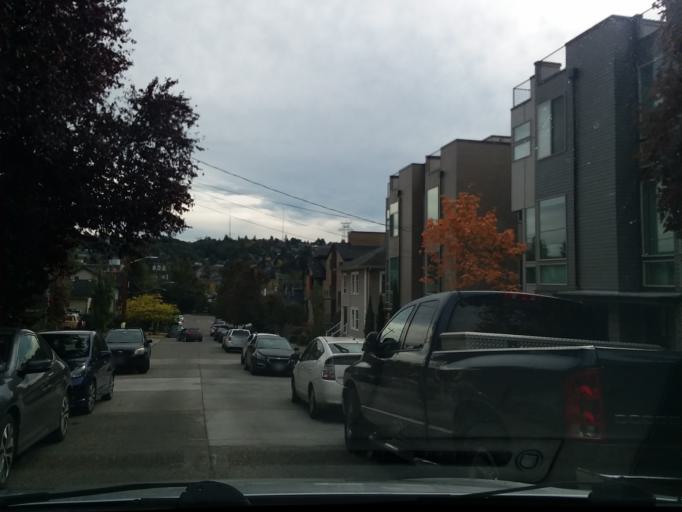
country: US
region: Washington
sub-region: King County
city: Seattle
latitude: 47.6533
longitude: -122.3524
